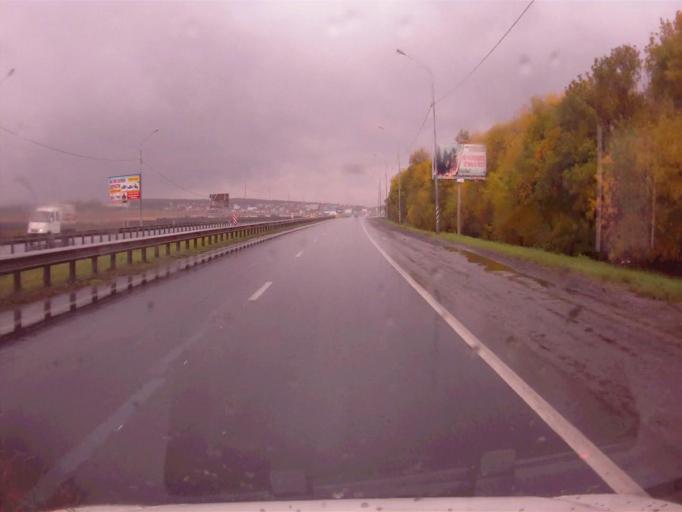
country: RU
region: Chelyabinsk
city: Dolgoderevenskoye
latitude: 55.2686
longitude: 61.3449
